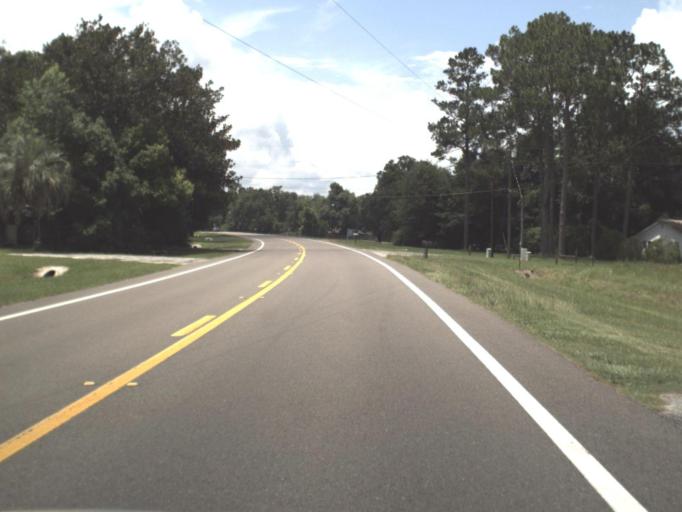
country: US
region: Florida
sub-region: Union County
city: Lake Butler
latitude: 30.0017
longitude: -82.3478
